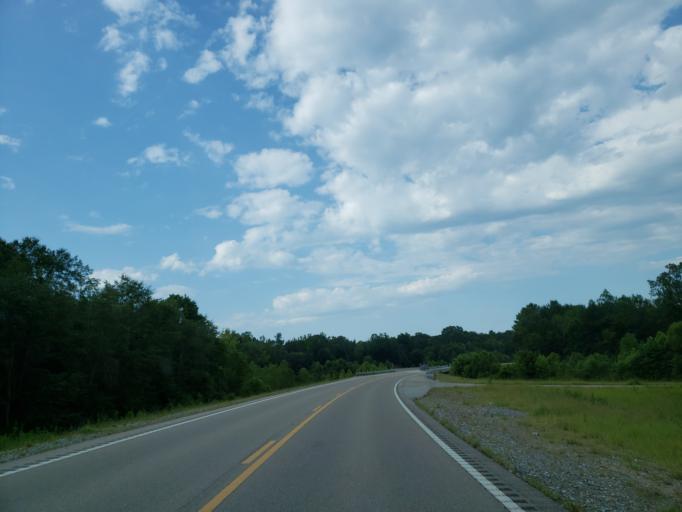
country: US
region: Mississippi
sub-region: Clarke County
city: Stonewall
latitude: 32.1763
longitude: -88.9282
